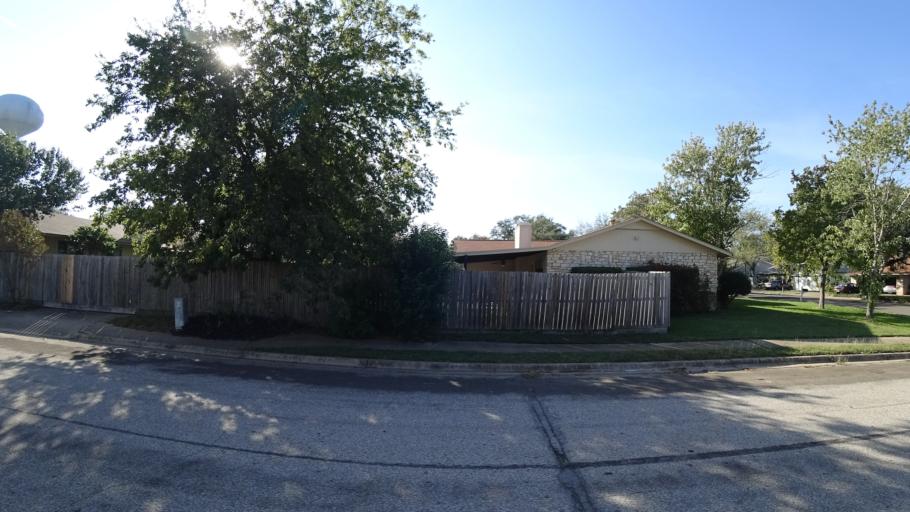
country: US
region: Texas
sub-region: Williamson County
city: Anderson Mill
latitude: 30.4555
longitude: -97.8136
